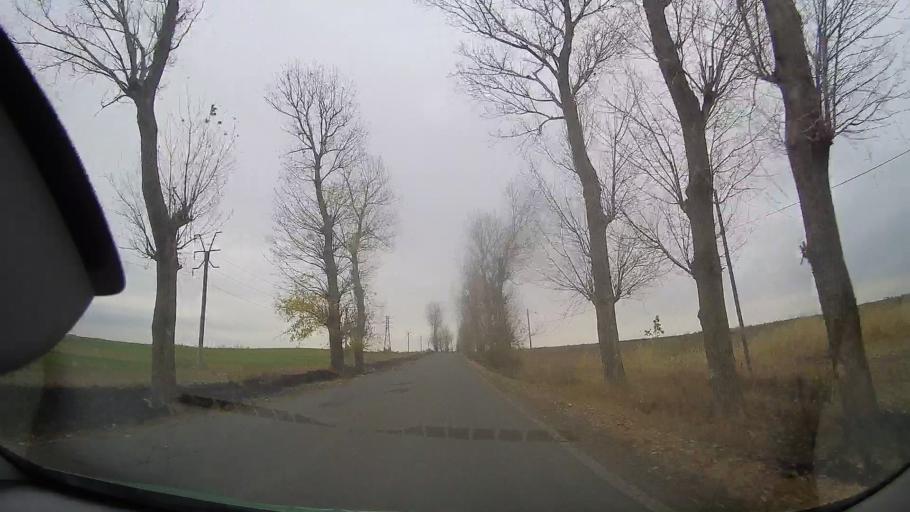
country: RO
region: Buzau
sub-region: Comuna Rusetu
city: Rusetu
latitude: 44.9493
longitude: 27.2283
